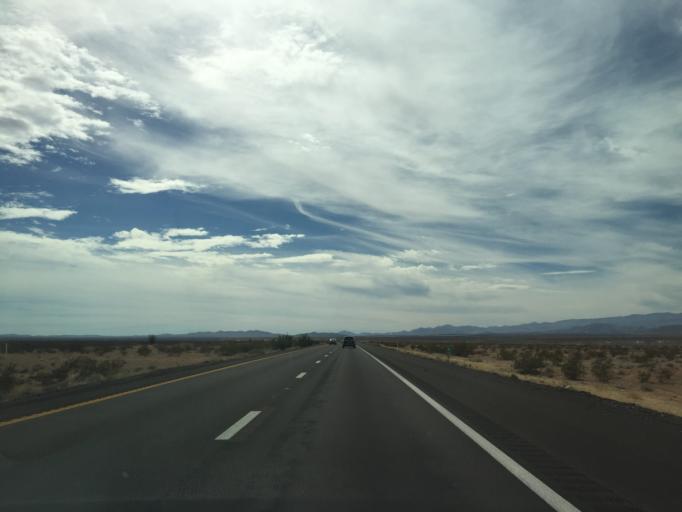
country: US
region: Nevada
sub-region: Clark County
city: Moapa Town
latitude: 36.5747
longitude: -114.6651
